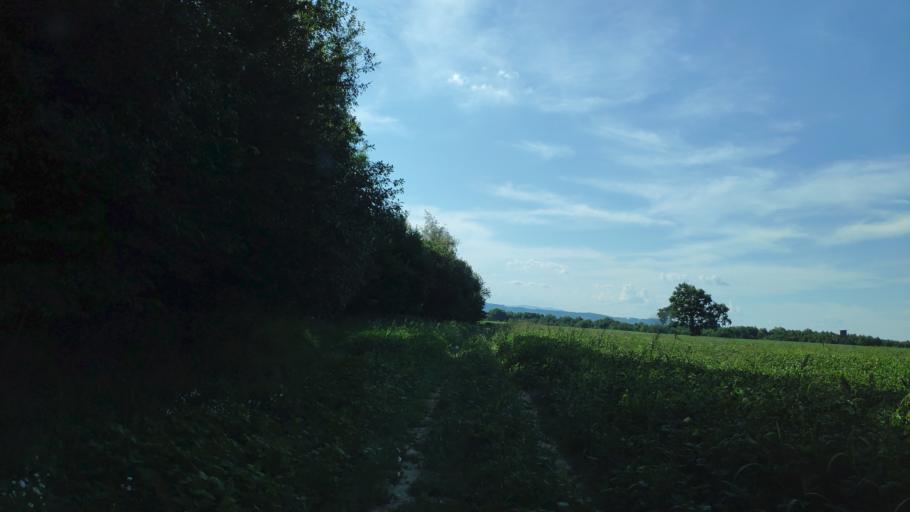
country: SK
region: Presovsky
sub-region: Okres Presov
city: Presov
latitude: 48.9061
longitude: 21.2948
